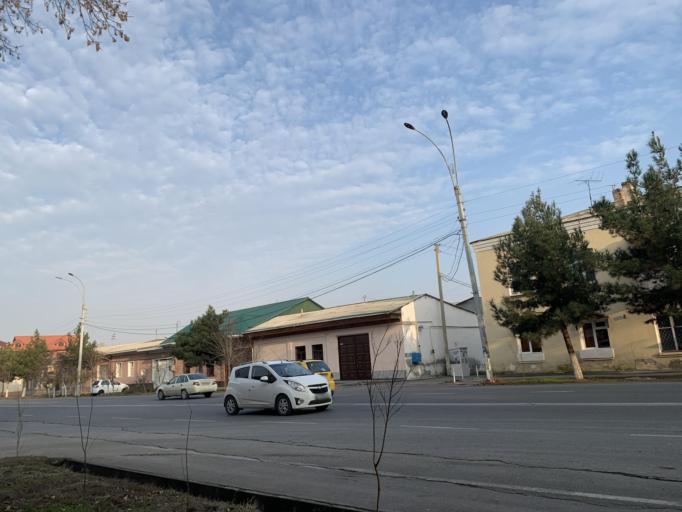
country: UZ
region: Fergana
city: Qo`qon
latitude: 40.5421
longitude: 70.9239
